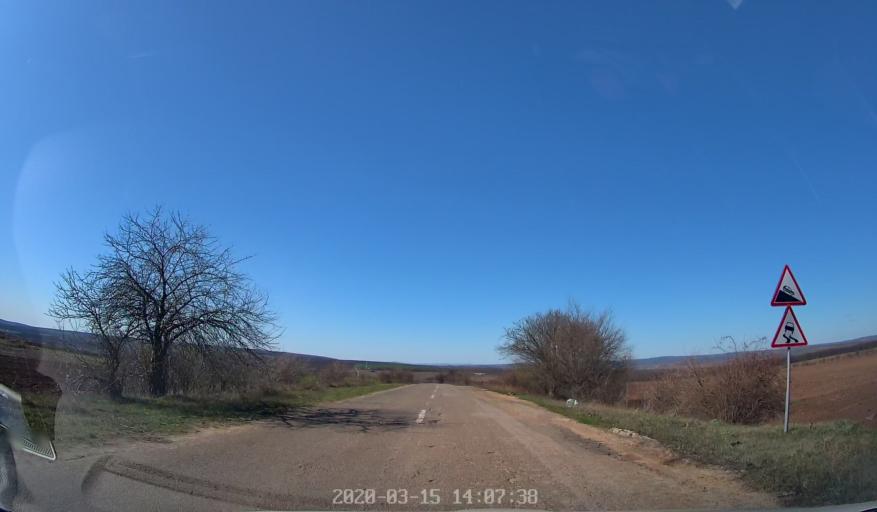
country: MD
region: Orhei
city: Orhei
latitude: 47.3040
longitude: 28.9462
